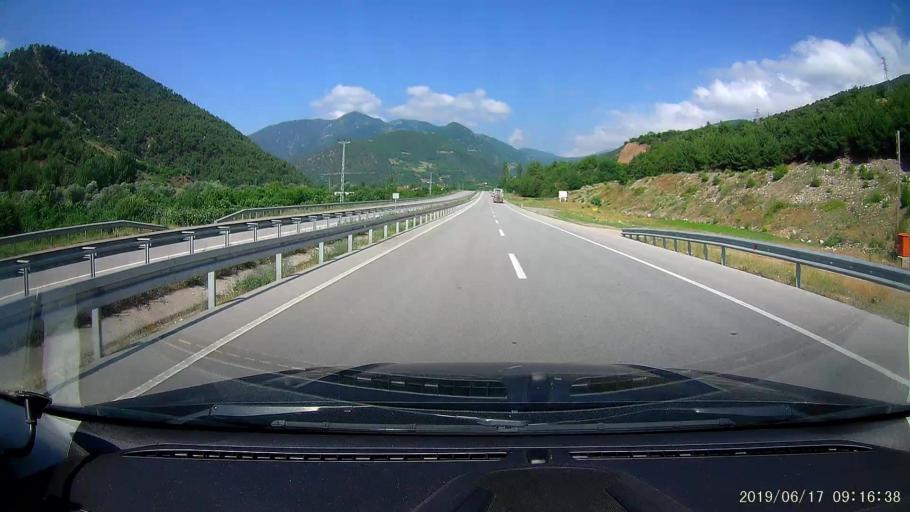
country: TR
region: Amasya
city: Akdag
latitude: 40.7444
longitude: 36.0066
